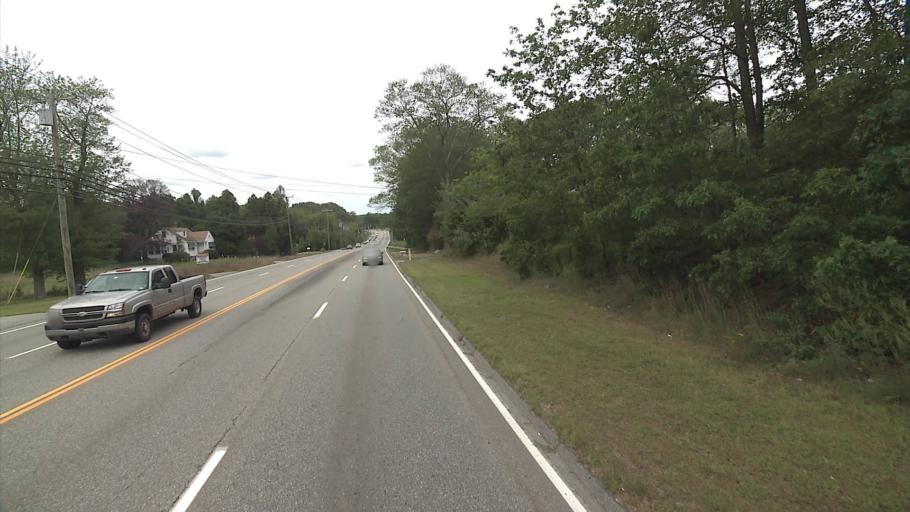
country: US
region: Connecticut
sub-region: New London County
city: Central Waterford
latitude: 41.3894
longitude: -72.1607
